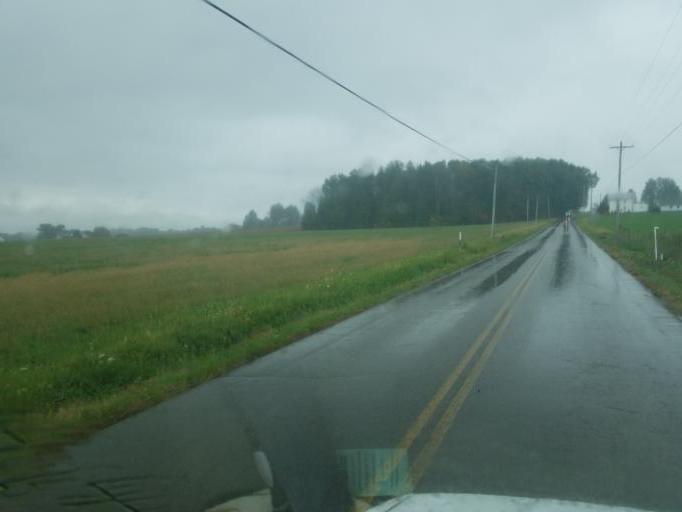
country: US
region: Ohio
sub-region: Wayne County
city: Shreve
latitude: 40.6441
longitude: -82.0212
